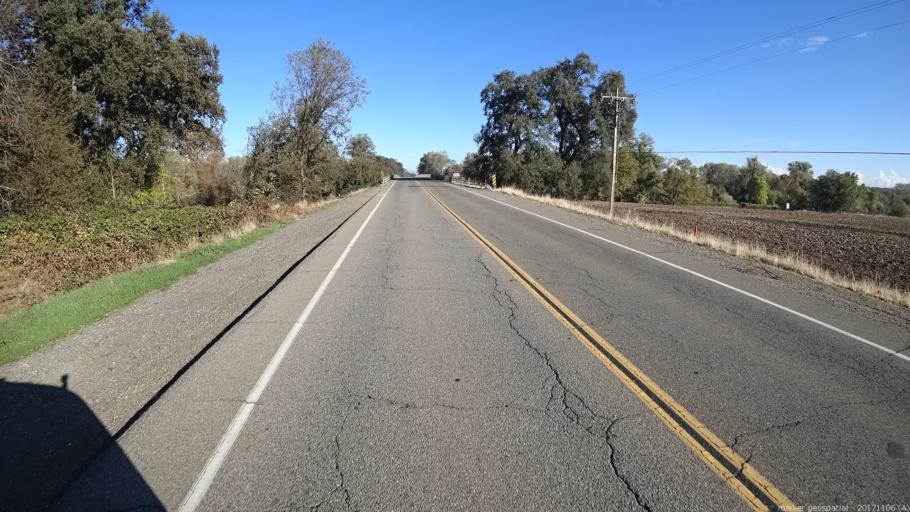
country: US
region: California
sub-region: Shasta County
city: Anderson
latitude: 40.4614
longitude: -122.2441
